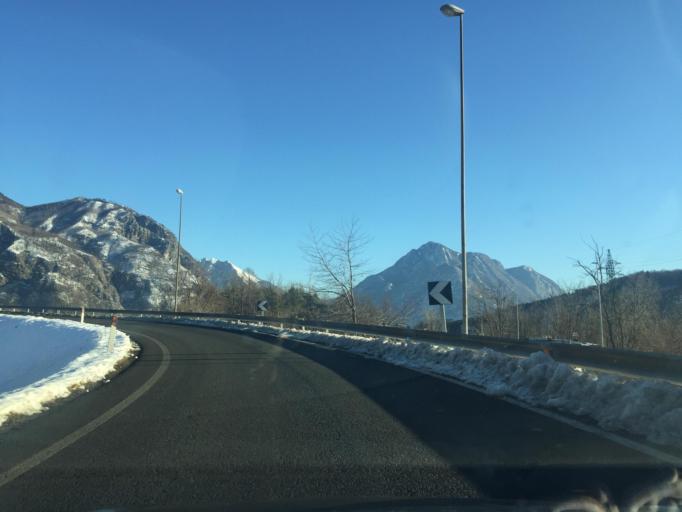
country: IT
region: Friuli Venezia Giulia
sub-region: Provincia di Udine
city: Tolmezzo
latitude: 46.3878
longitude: 13.0283
